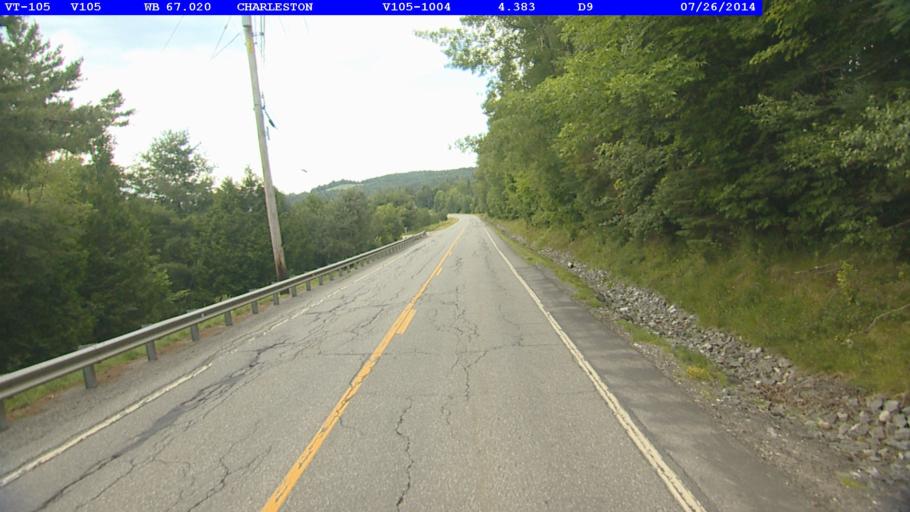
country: US
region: Vermont
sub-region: Orleans County
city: Newport
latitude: 44.8575
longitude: -72.0349
